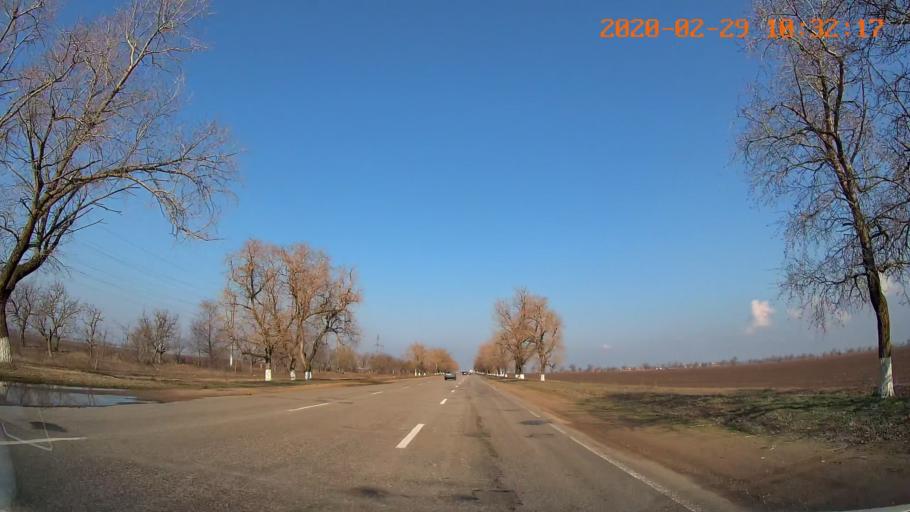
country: UA
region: Odessa
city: Velykoploske
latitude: 46.9592
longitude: 29.5551
